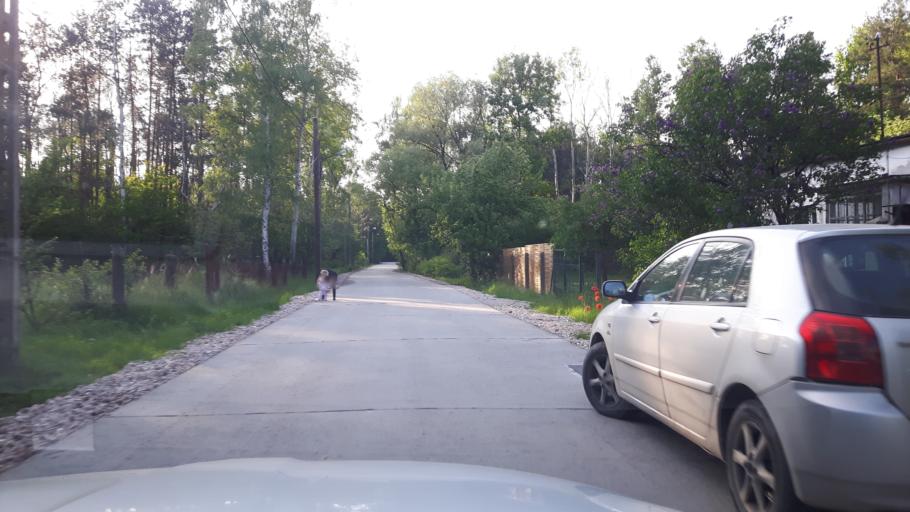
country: PL
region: Masovian Voivodeship
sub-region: Warszawa
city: Rembertow
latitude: 52.2763
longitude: 21.1554
